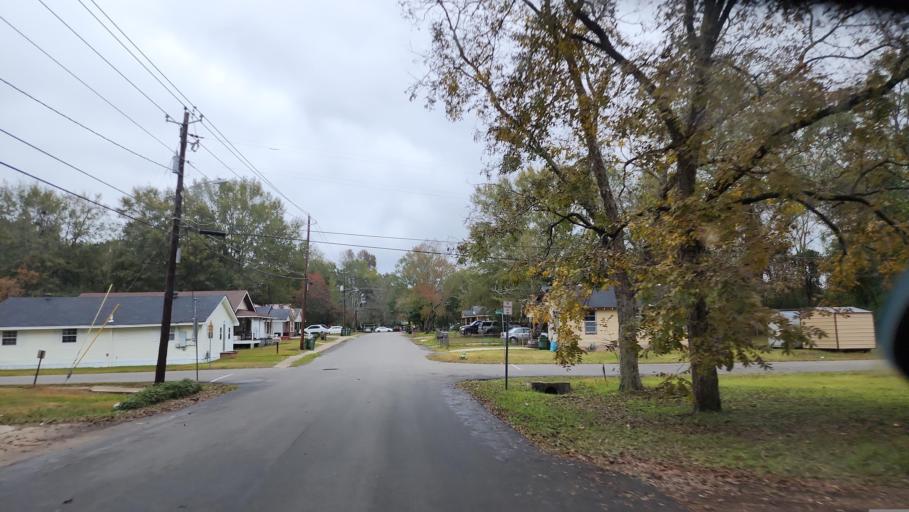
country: US
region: Mississippi
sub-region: Forrest County
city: Hattiesburg
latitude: 31.3057
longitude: -89.3015
